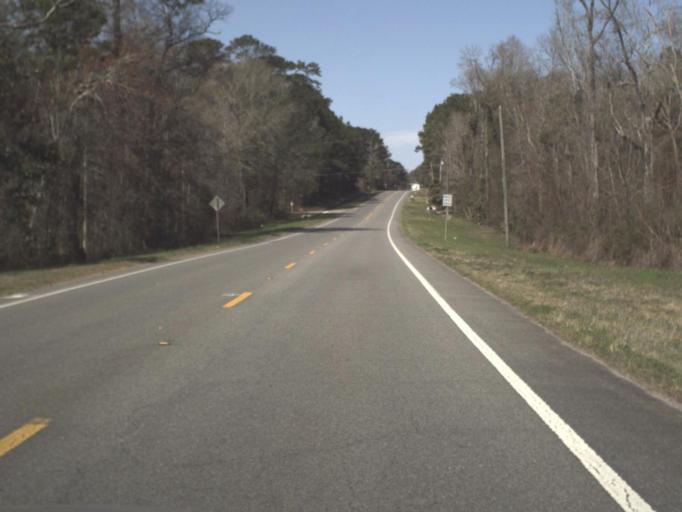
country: US
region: Florida
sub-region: Gadsden County
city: Quincy
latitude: 30.5945
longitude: -84.5302
